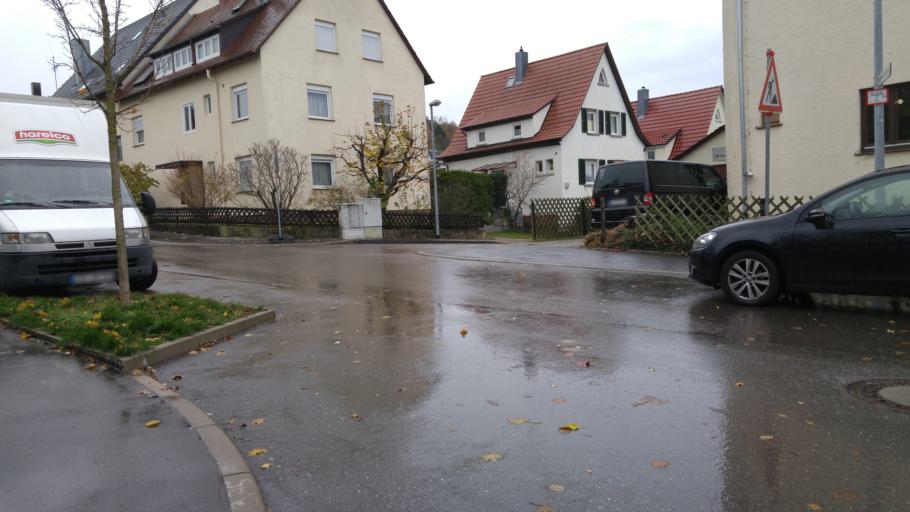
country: DE
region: Baden-Wuerttemberg
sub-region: Regierungsbezirk Stuttgart
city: Leonberg
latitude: 48.8044
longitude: 9.0181
